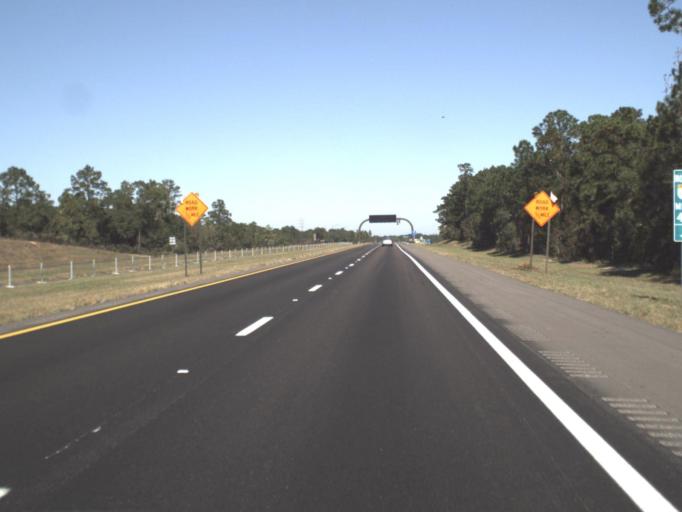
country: US
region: Florida
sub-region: Hernando County
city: Brookridge
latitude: 28.5198
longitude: -82.4778
